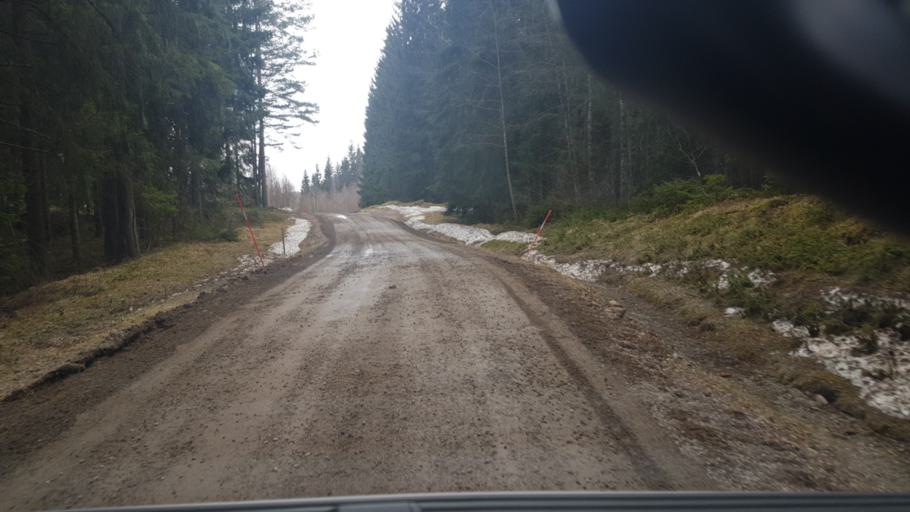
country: SE
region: Vaermland
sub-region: Eda Kommun
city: Amotfors
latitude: 59.8093
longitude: 12.4159
